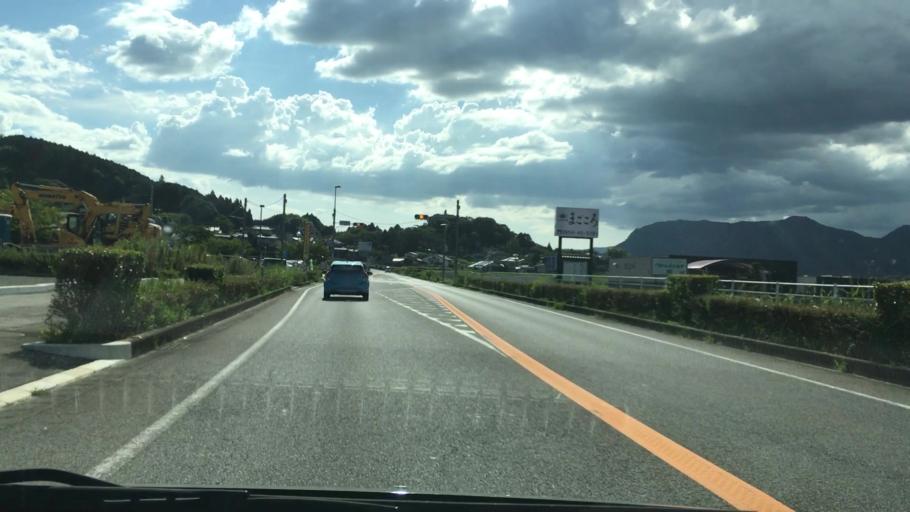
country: JP
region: Saga Prefecture
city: Takeocho-takeo
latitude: 33.1923
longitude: 129.9575
